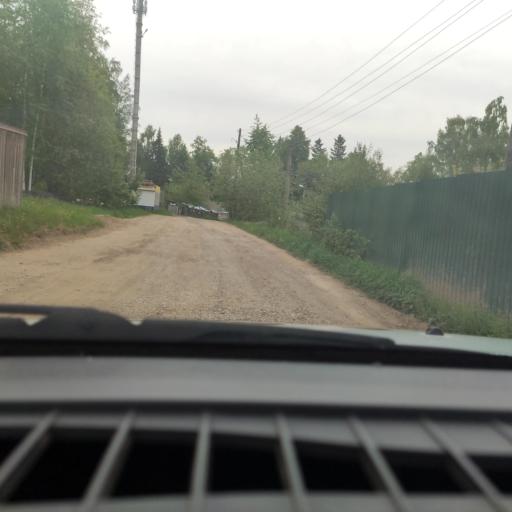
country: RU
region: Perm
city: Novyye Lyady
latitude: 57.8912
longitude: 56.6603
